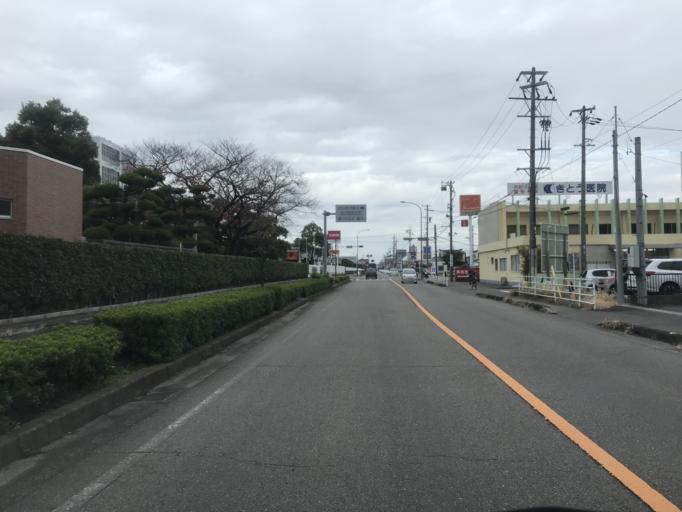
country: JP
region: Aichi
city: Nagoya-shi
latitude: 35.2094
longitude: 136.8540
